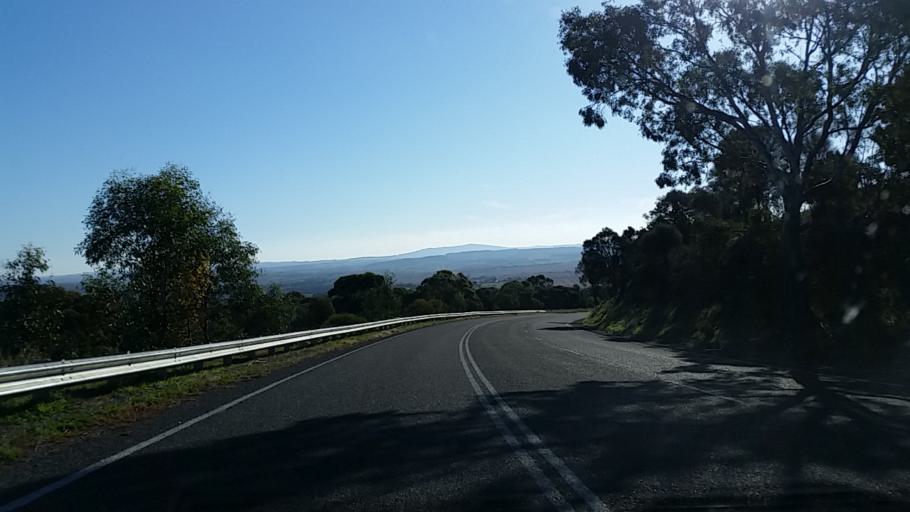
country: AU
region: South Australia
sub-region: Mount Barker
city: Callington
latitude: -35.1144
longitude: 139.0674
